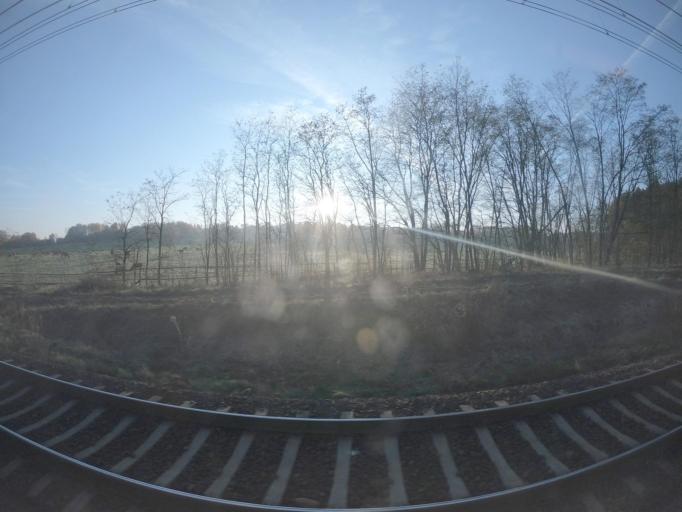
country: PL
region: Lubusz
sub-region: Powiat slubicki
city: Rzepin
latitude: 52.2599
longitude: 14.9453
